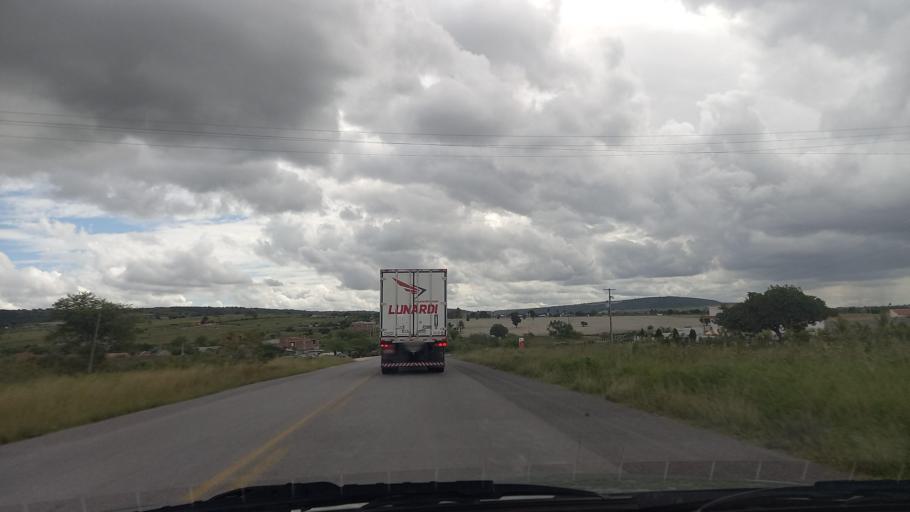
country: BR
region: Pernambuco
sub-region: Lajedo
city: Lajedo
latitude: -8.6643
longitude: -36.3564
